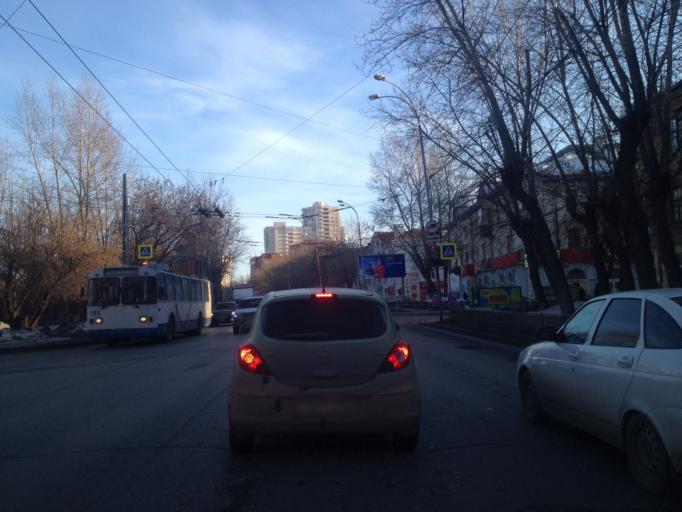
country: RU
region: Sverdlovsk
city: Yekaterinburg
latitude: 56.8076
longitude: 60.6240
